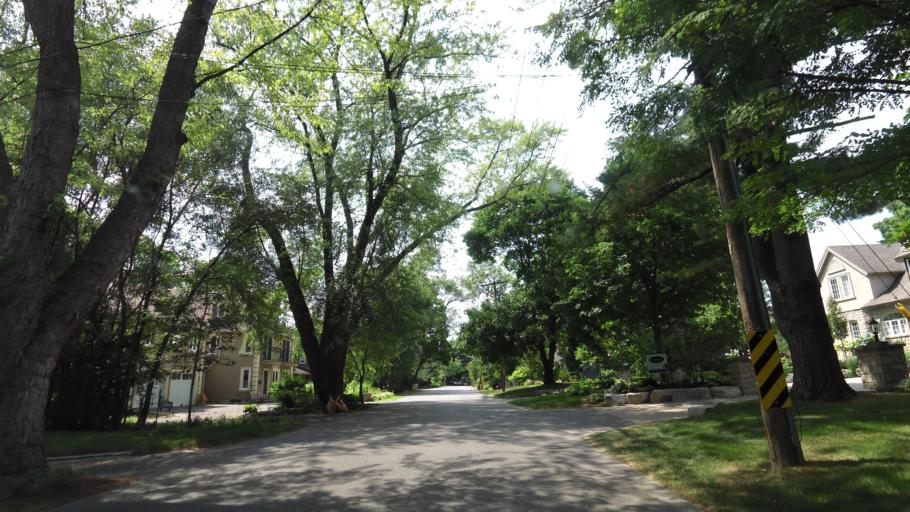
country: CA
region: Ontario
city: Mississauga
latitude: 43.5538
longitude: -79.5925
